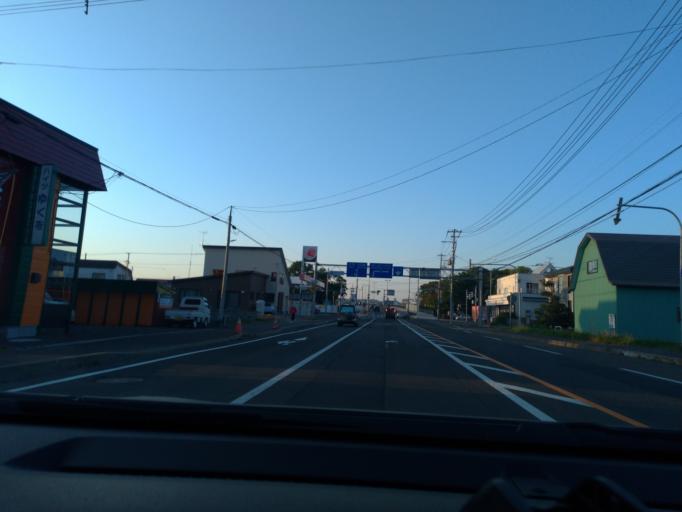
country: JP
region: Hokkaido
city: Tobetsu
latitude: 43.2111
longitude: 141.5184
